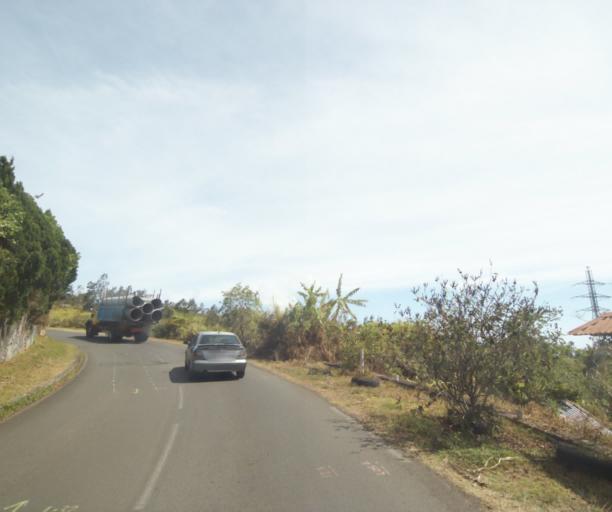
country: RE
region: Reunion
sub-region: Reunion
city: Saint-Paul
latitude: -21.0402
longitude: 55.3187
